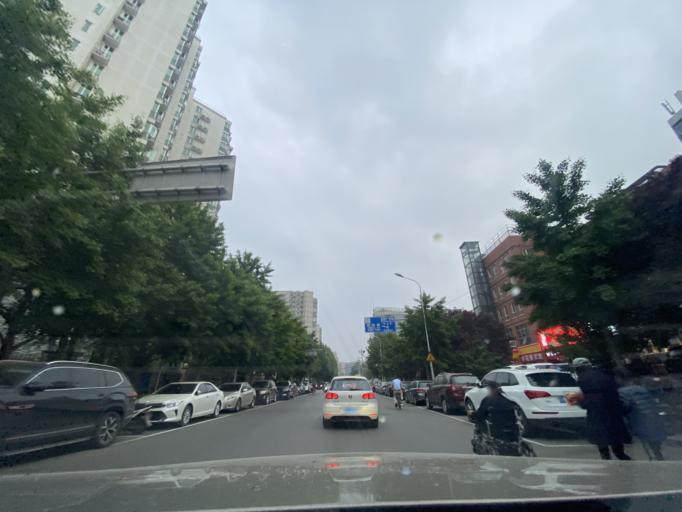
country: CN
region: Beijing
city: Sijiqing
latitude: 39.9588
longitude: 116.2744
